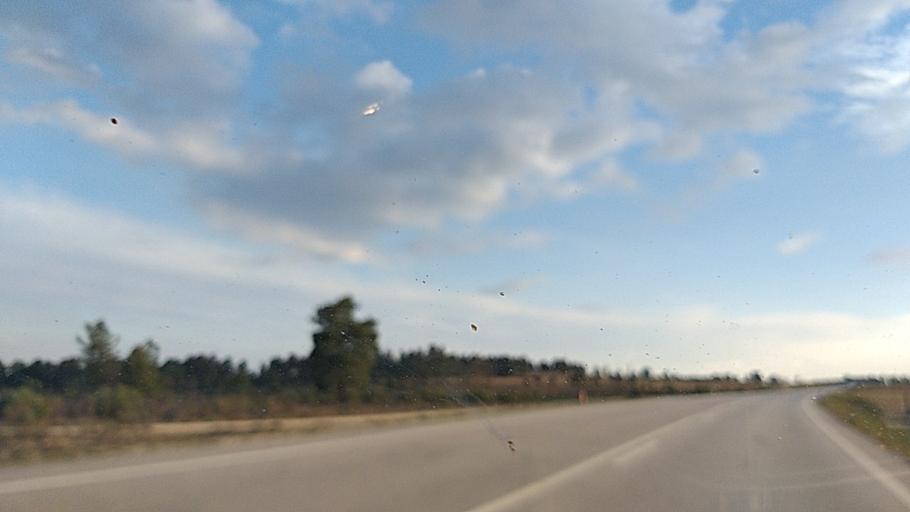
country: PT
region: Guarda
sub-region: Pinhel
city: Pinhel
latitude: 40.6553
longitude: -6.9665
